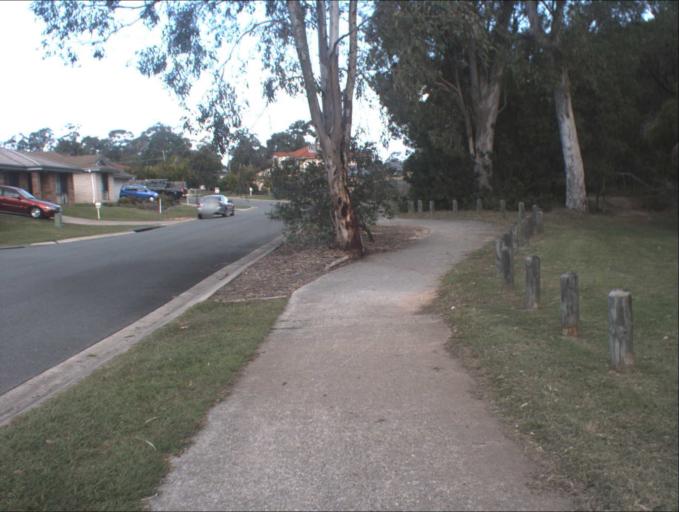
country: AU
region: Queensland
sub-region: Logan
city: Park Ridge South
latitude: -27.6842
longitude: 153.0568
